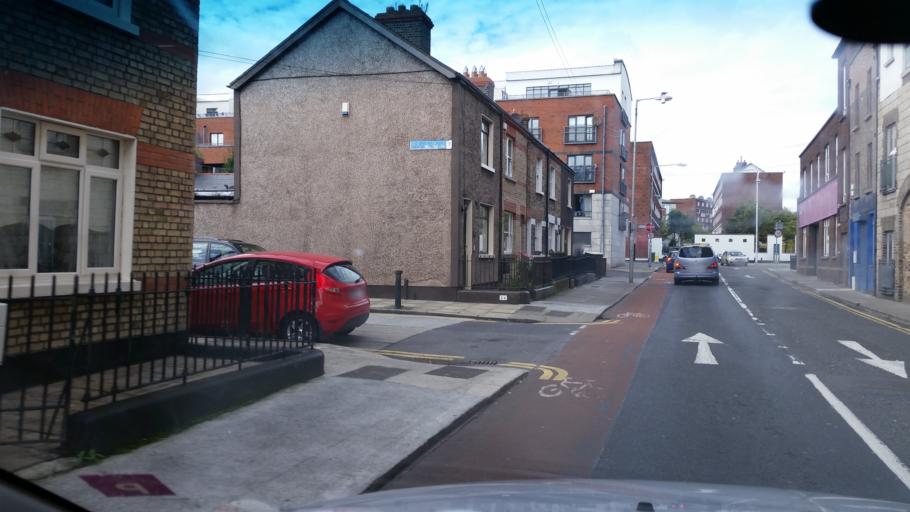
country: IE
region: Leinster
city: Rialto
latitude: 53.3494
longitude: -6.2735
